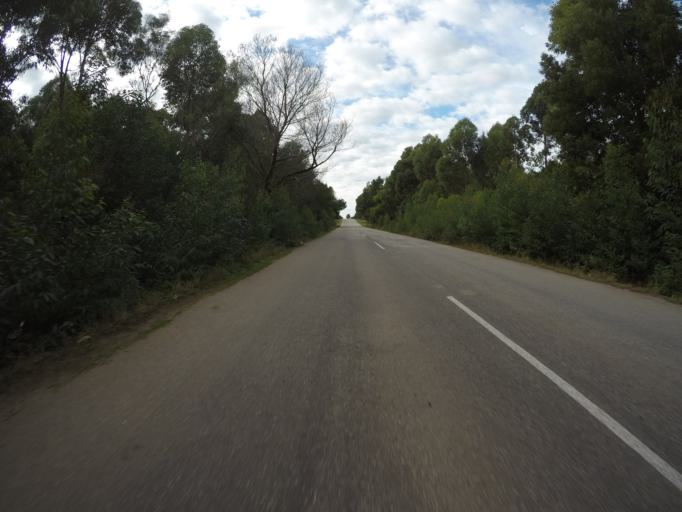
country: ZA
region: Eastern Cape
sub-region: Cacadu District Municipality
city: Kareedouw
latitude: -34.0234
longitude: 24.3624
